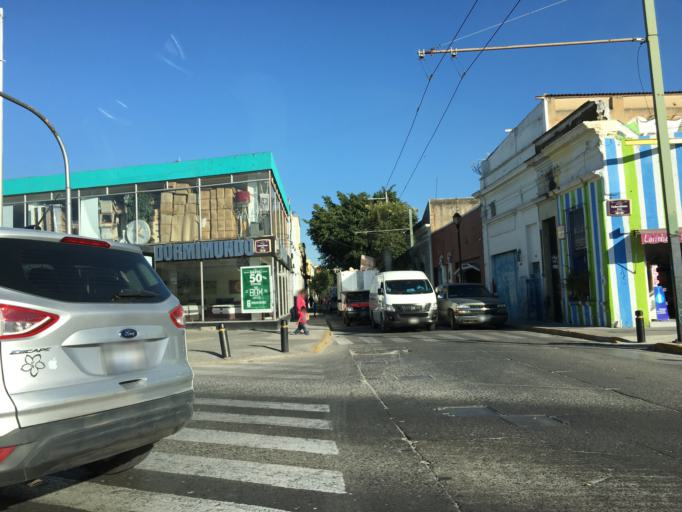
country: MX
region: Jalisco
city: Guadalajara
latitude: 20.6781
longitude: -103.3543
